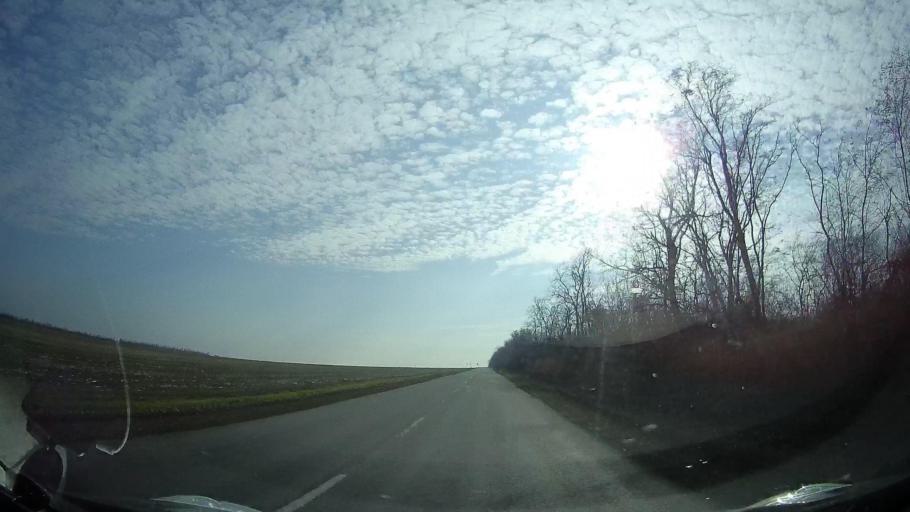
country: RU
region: Rostov
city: Veselyy
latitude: 46.9953
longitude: 40.7200
